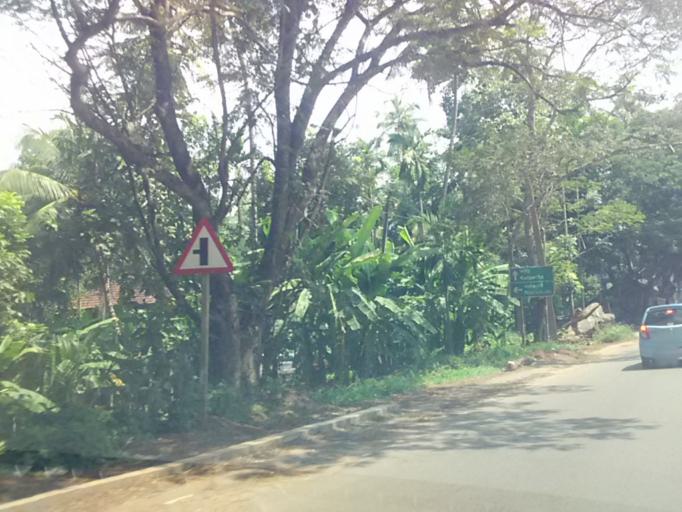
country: IN
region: Kerala
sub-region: Kozhikode
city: Kunnamangalam
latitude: 11.3332
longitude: 75.8921
